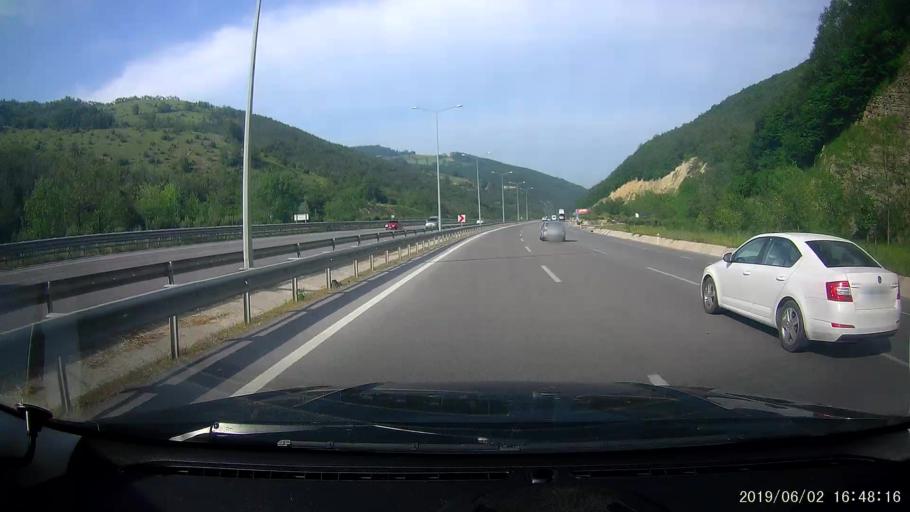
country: TR
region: Samsun
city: Kavak
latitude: 41.2250
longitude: 36.1316
